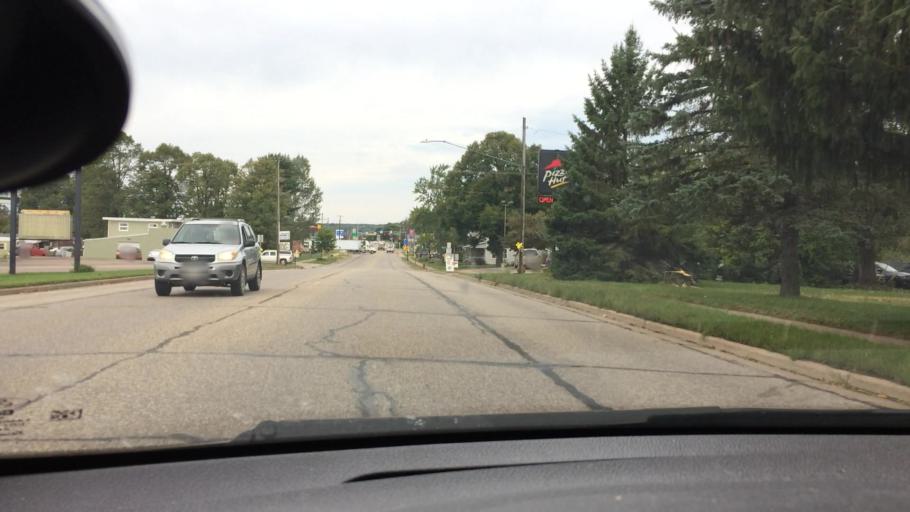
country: US
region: Wisconsin
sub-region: Clark County
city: Neillsville
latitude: 44.5527
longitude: -90.5920
